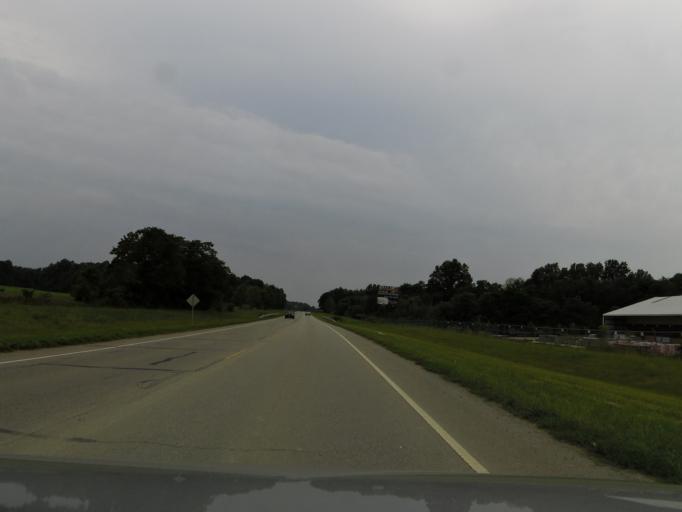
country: US
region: Ohio
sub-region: Brown County
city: Georgetown
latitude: 38.8955
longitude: -83.8998
